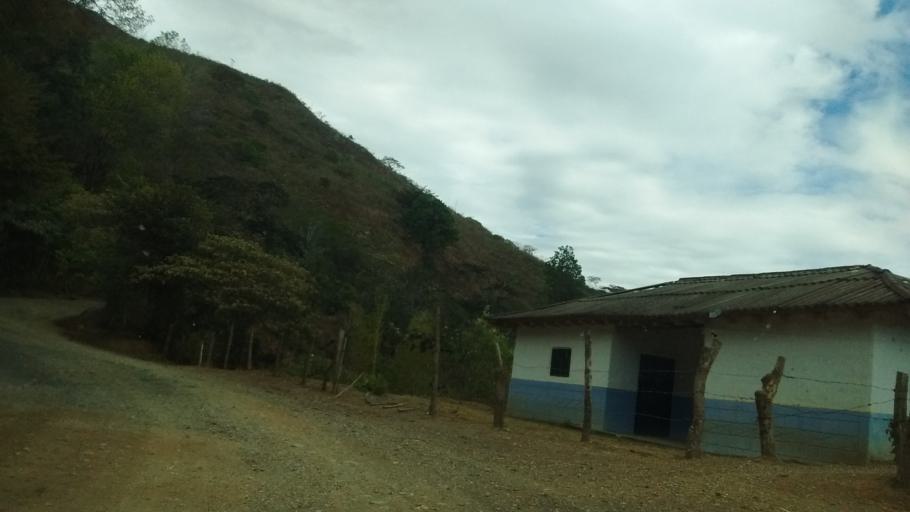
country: CO
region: Cauca
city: Almaguer
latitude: 1.8447
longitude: -76.8975
